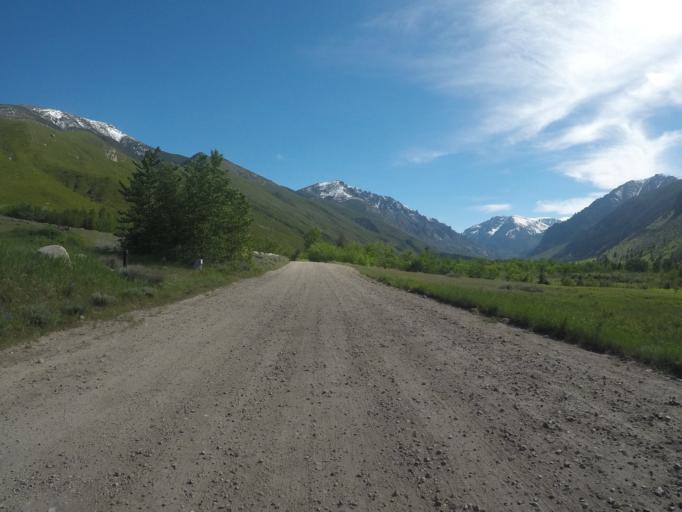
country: US
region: Montana
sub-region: Stillwater County
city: Absarokee
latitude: 45.2607
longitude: -109.5649
